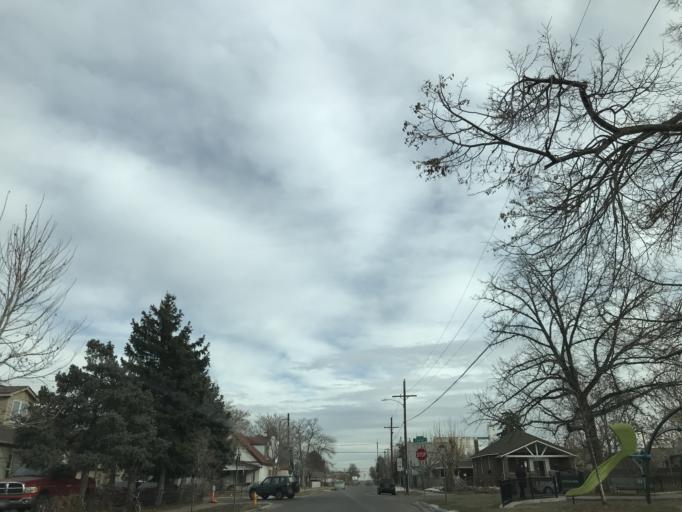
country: US
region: Colorado
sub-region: Adams County
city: Commerce City
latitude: 39.7789
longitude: -104.9547
